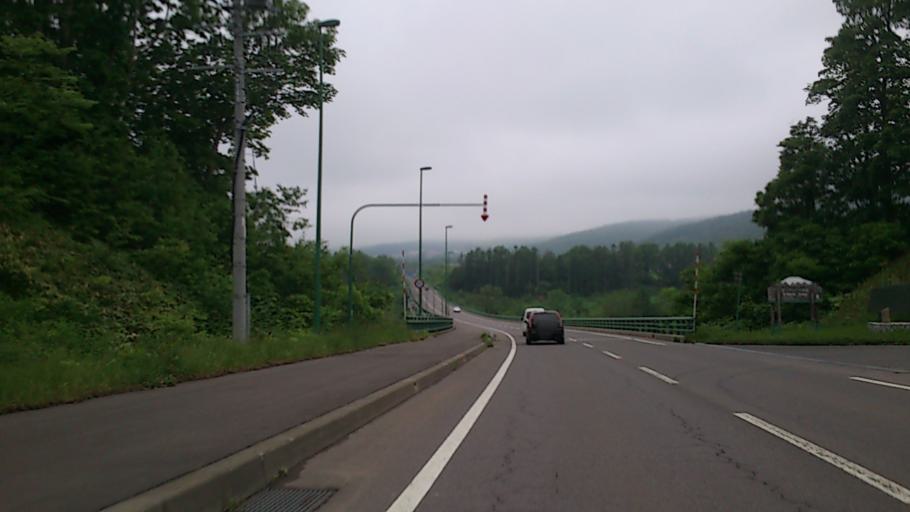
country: JP
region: Hokkaido
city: Niseko Town
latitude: 42.8652
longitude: 140.7351
